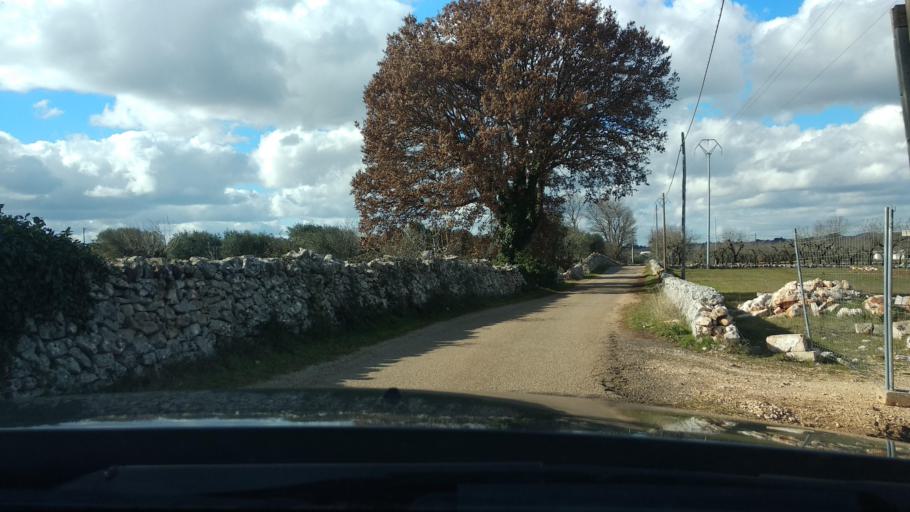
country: IT
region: Apulia
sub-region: Provincia di Brindisi
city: Casalini
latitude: 40.7055
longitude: 17.4546
